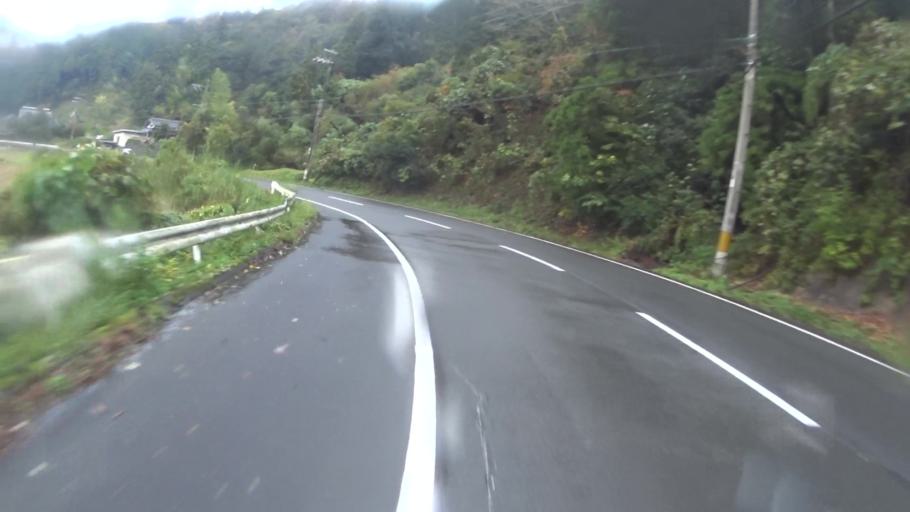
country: JP
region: Kyoto
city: Miyazu
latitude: 35.4780
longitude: 135.2409
